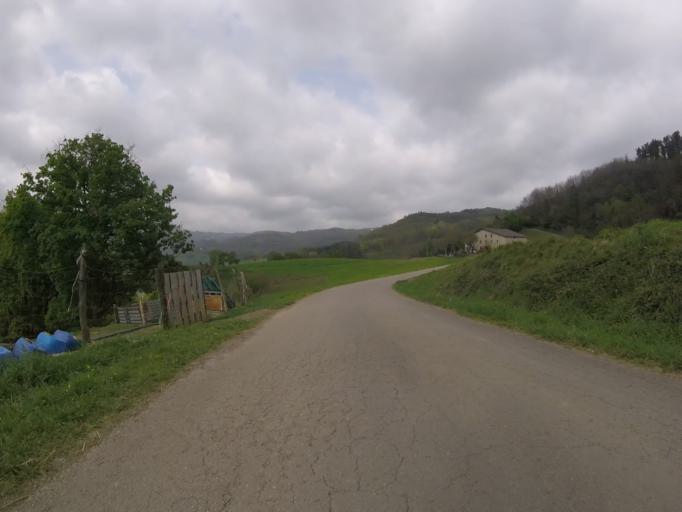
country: ES
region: Basque Country
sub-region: Provincia de Guipuzcoa
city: Zizurkil
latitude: 43.2099
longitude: -2.0809
